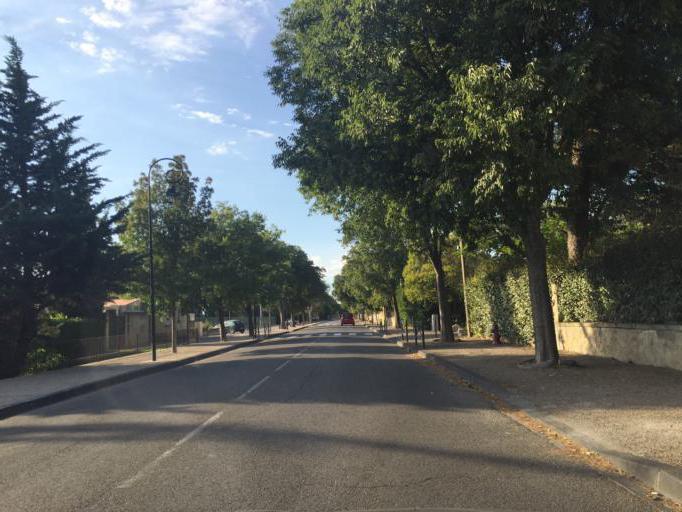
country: FR
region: Provence-Alpes-Cote d'Azur
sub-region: Departement du Vaucluse
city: Pernes-les-Fontaines
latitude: 44.0015
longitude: 5.0580
